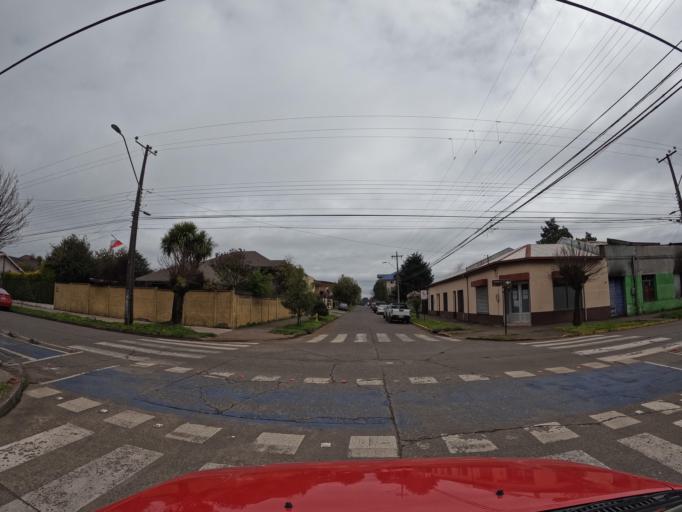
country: CL
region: Araucania
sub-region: Provincia de Malleco
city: Victoria
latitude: -38.2313
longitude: -72.3295
